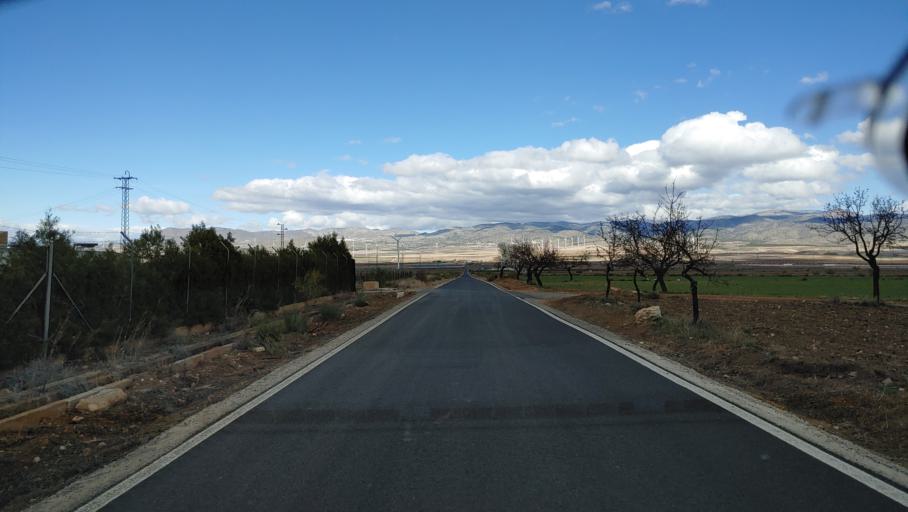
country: ES
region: Andalusia
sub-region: Provincia de Granada
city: Hueneja
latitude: 37.1927
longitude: -2.9549
